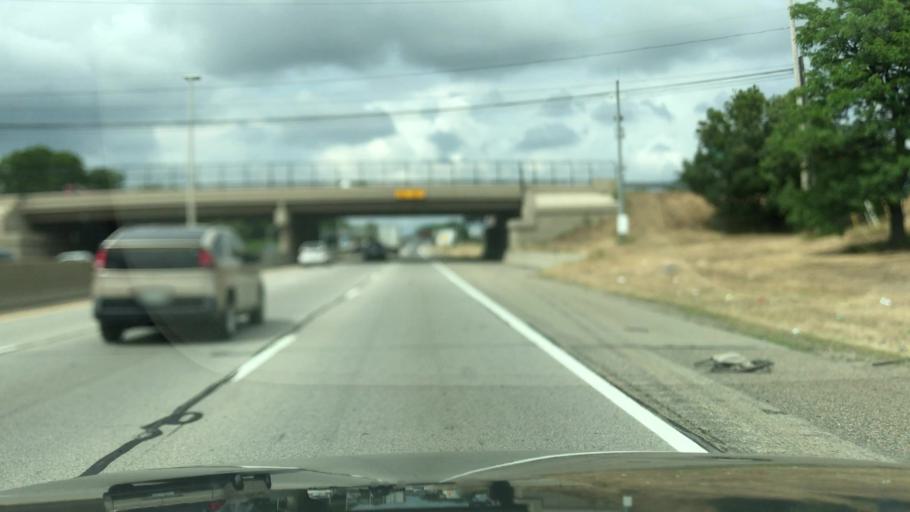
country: US
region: Michigan
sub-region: Kent County
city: Wyoming
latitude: 42.8980
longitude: -85.6776
